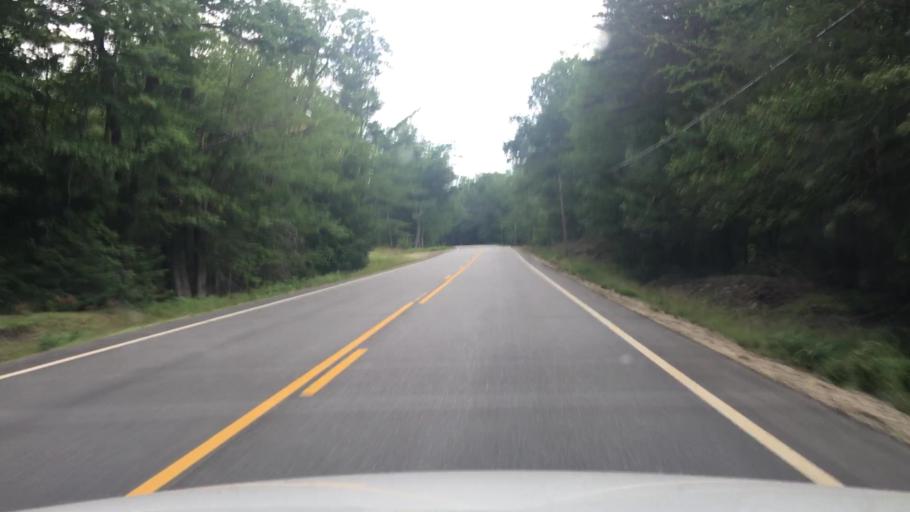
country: US
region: Maine
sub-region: Oxford County
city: Hartford
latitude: 44.3735
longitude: -70.4035
